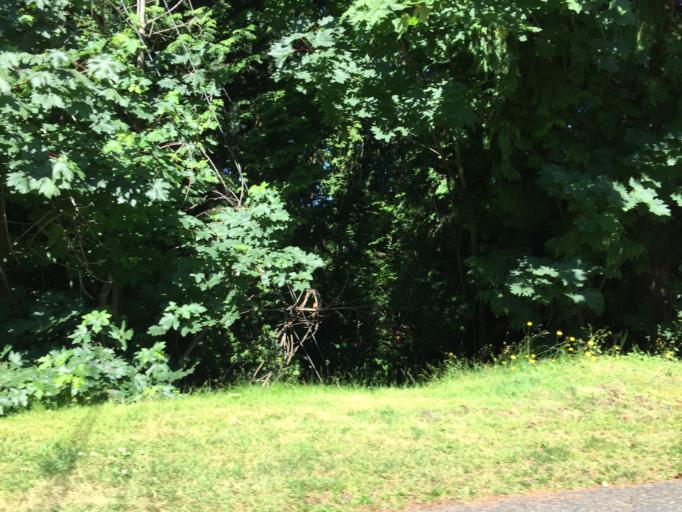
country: US
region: Washington
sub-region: King County
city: Bellevue
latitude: 47.6242
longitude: -122.1936
